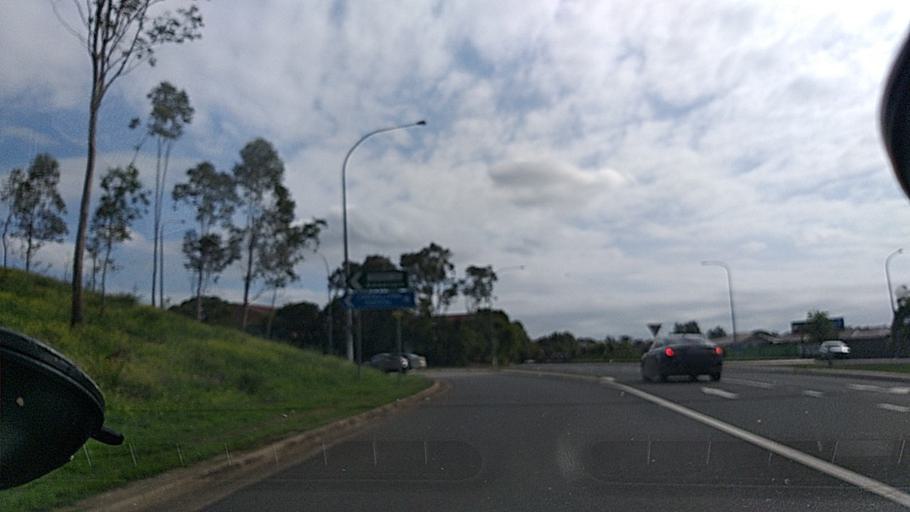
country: AU
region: New South Wales
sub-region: Campbelltown Municipality
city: Glen Alpine
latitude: -34.0785
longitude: 150.7983
